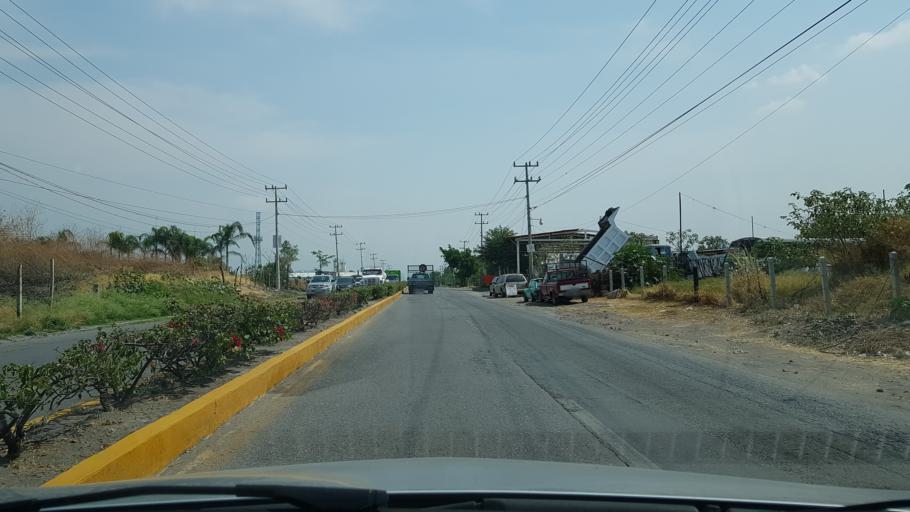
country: MX
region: Morelos
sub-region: Xochitepec
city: Chiconcuac
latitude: 18.7993
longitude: -99.1990
